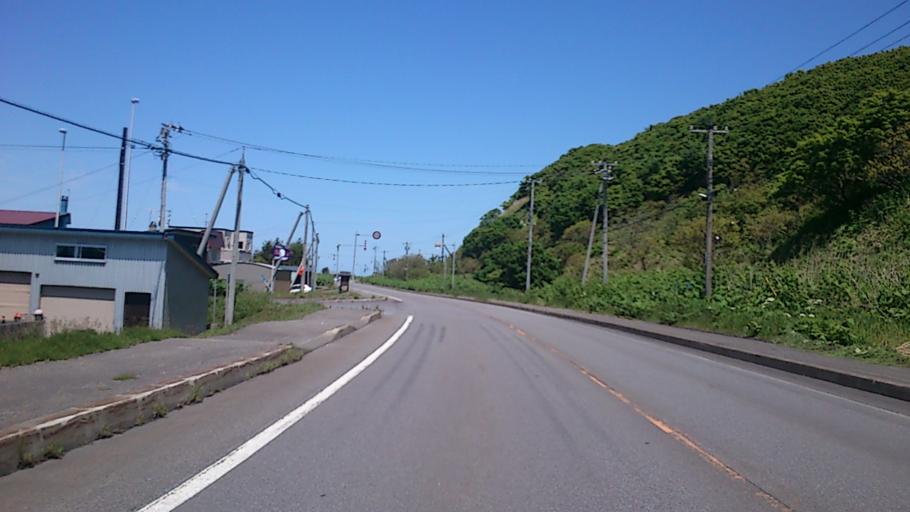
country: JP
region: Hokkaido
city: Rumoi
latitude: 43.9706
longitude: 141.6467
